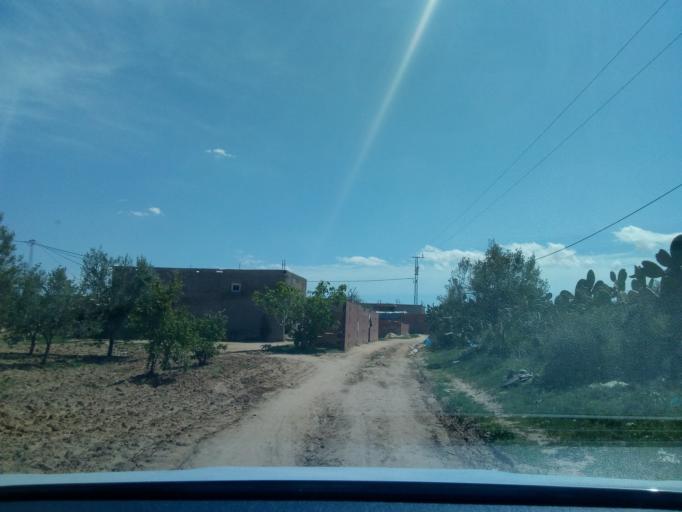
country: TN
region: Safaqis
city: Sfax
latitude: 34.7366
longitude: 10.4956
